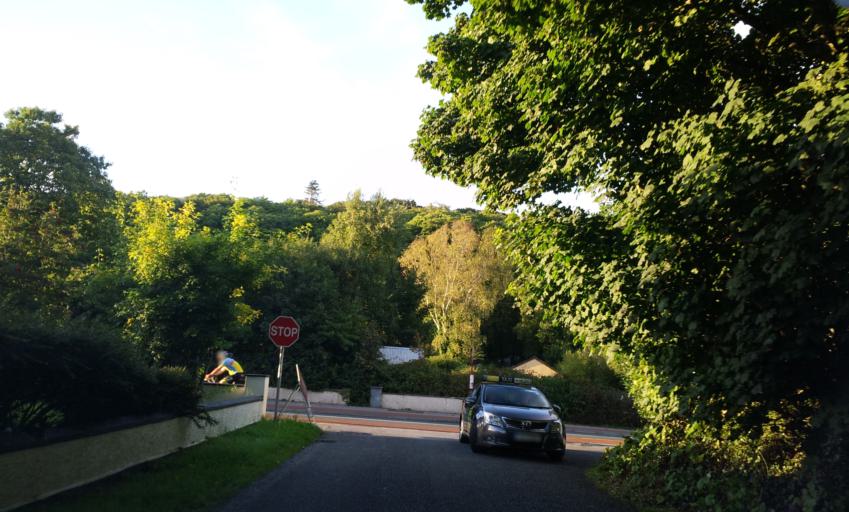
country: IE
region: Munster
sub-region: Ciarrai
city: Cill Airne
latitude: 52.0703
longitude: -9.5862
